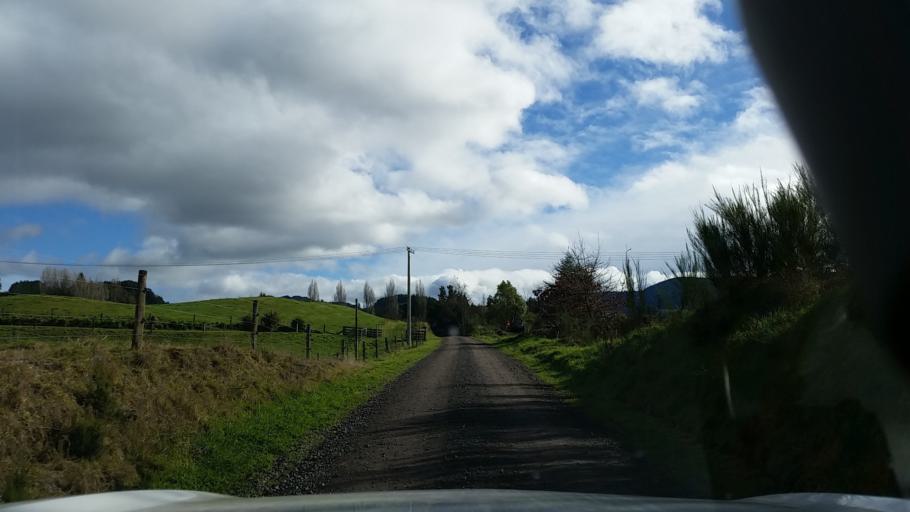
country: NZ
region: Bay of Plenty
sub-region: Rotorua District
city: Rotorua
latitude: -38.4443
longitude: 176.2849
